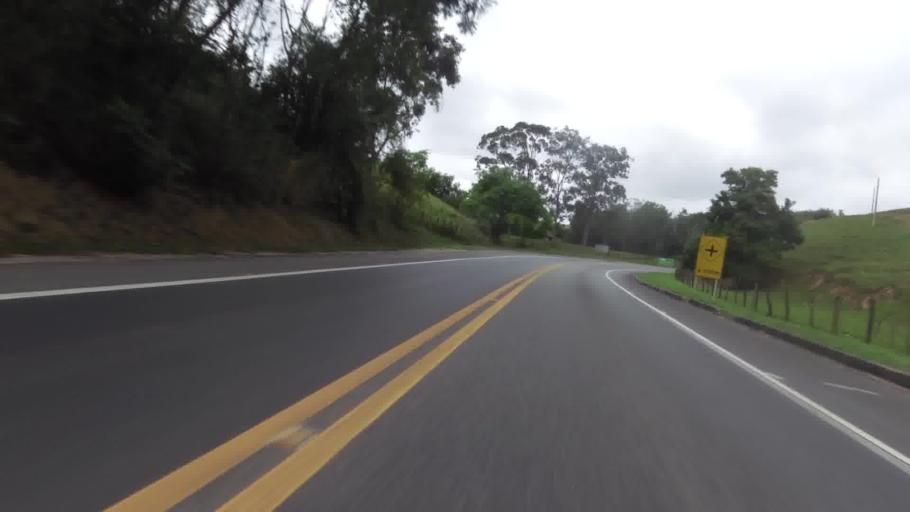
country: BR
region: Espirito Santo
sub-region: Iconha
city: Iconha
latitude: -20.7692
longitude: -40.7601
